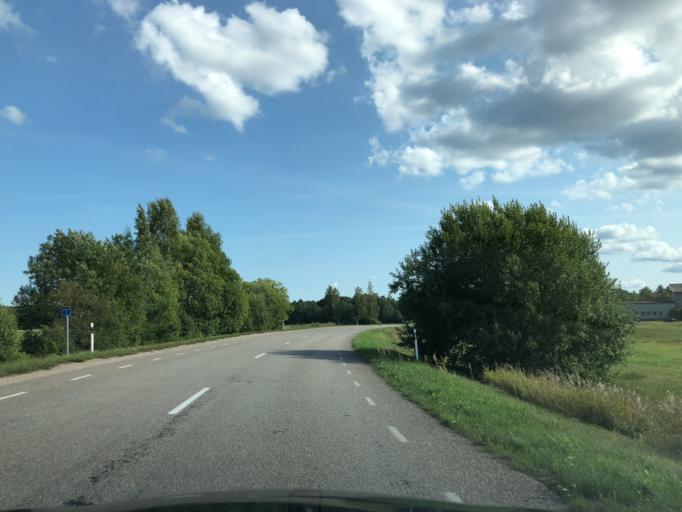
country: EE
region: Hiiumaa
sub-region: Kaerdla linn
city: Kardla
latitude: 58.7116
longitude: 22.5854
